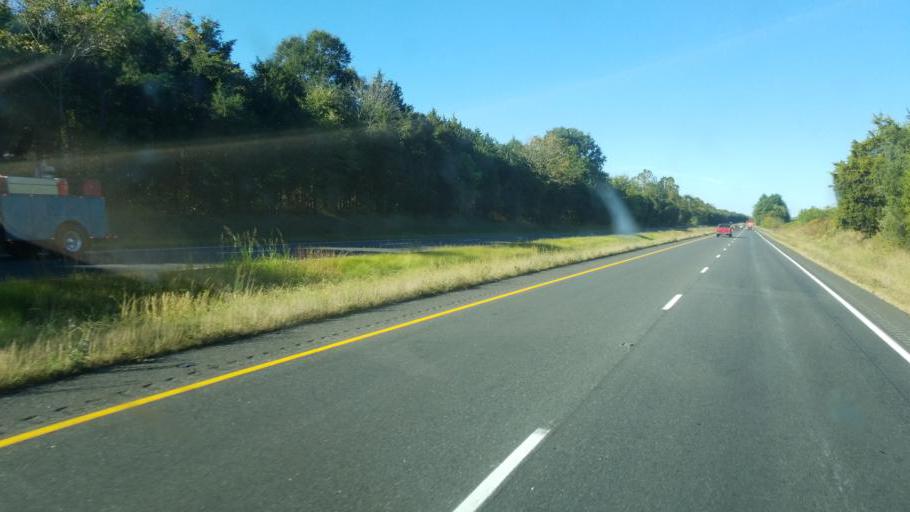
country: US
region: Virginia
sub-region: Culpeper County
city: Culpeper
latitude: 38.5069
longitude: -77.8758
